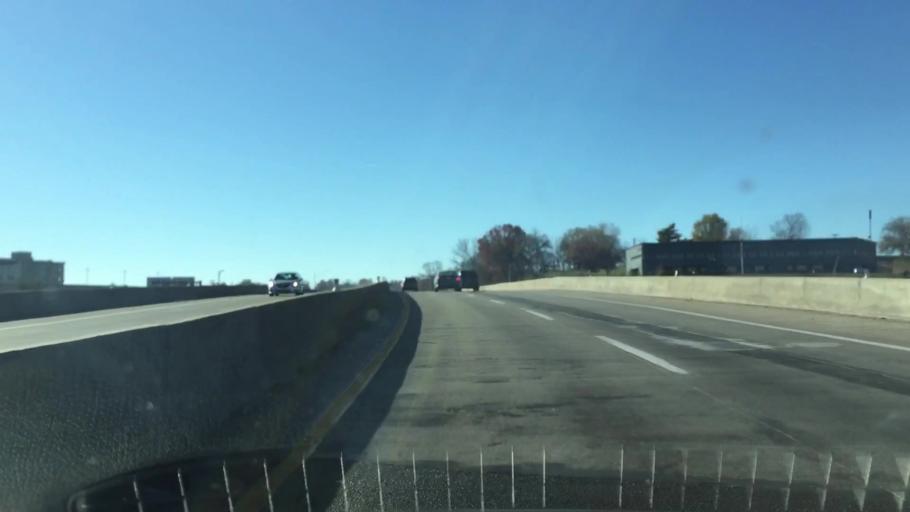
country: US
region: Missouri
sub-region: Cole County
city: Jefferson City
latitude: 38.5828
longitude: -92.1830
